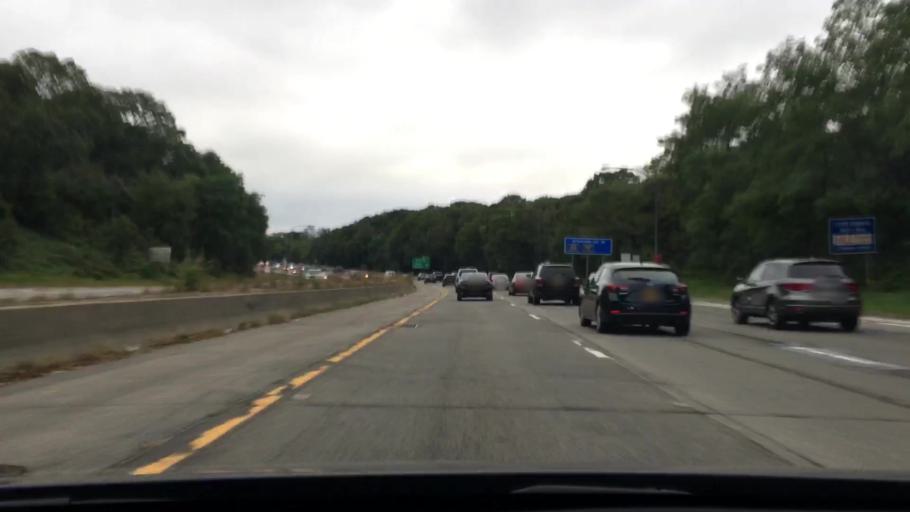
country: US
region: New York
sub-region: Nassau County
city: Roslyn Heights
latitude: 40.7815
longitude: -73.6439
